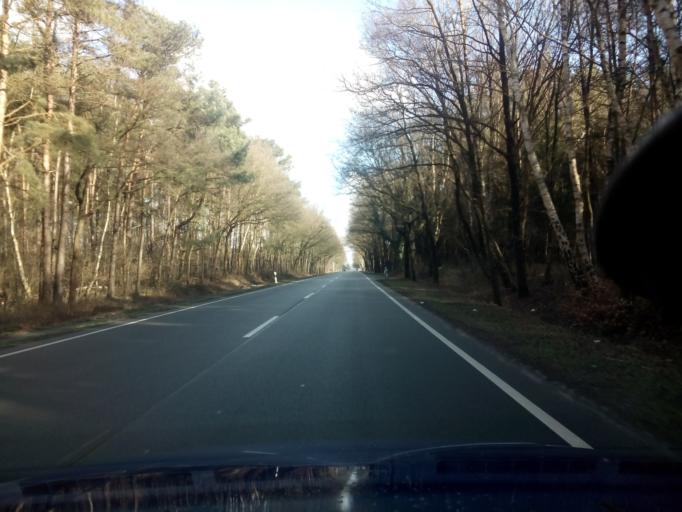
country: DE
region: Lower Saxony
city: Hambergen
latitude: 53.3129
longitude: 8.8539
